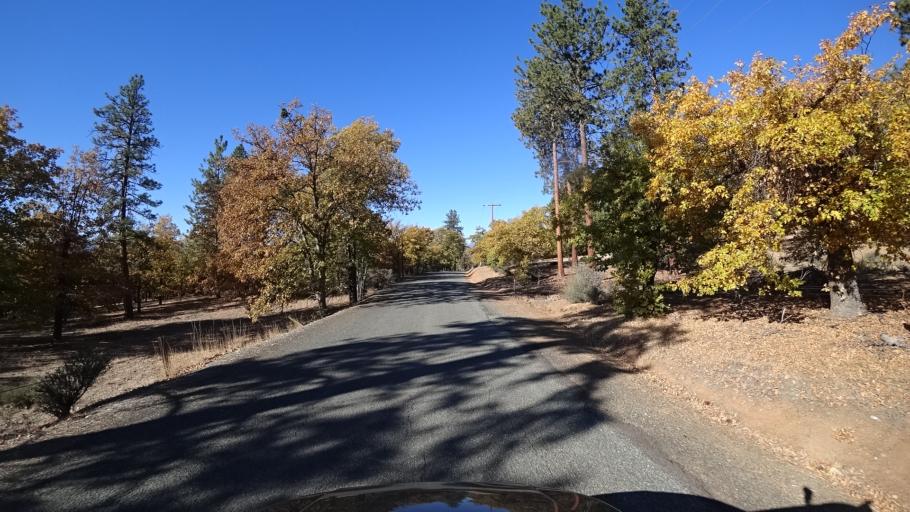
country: US
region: California
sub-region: Siskiyou County
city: Yreka
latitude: 41.5778
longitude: -122.8069
